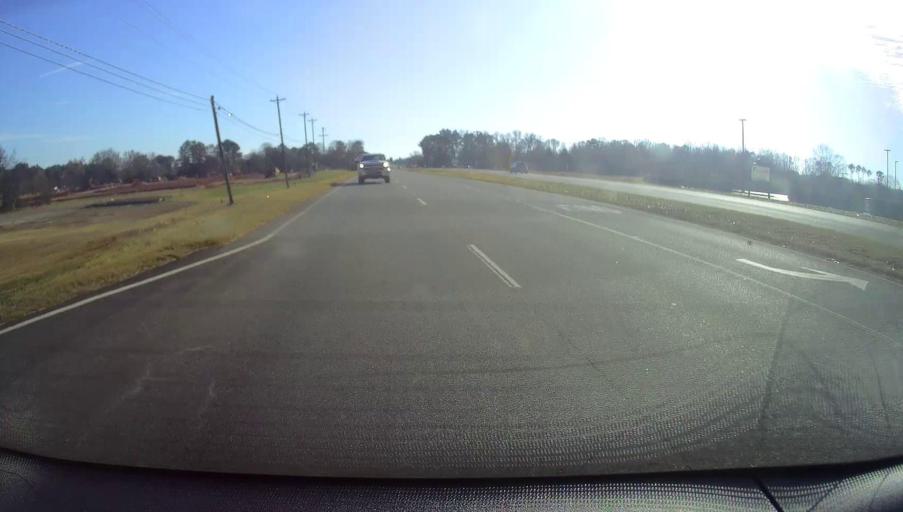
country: US
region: Alabama
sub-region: Limestone County
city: Athens
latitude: 34.7595
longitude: -86.9570
